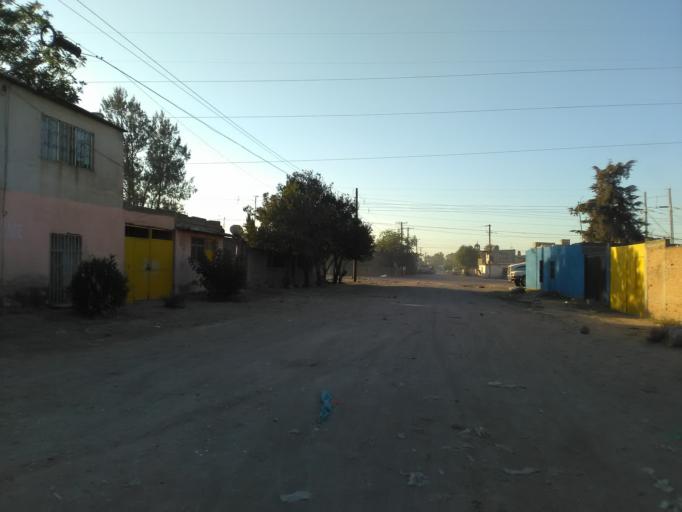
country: MX
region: Durango
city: Victoria de Durango
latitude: 24.0547
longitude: -104.6393
